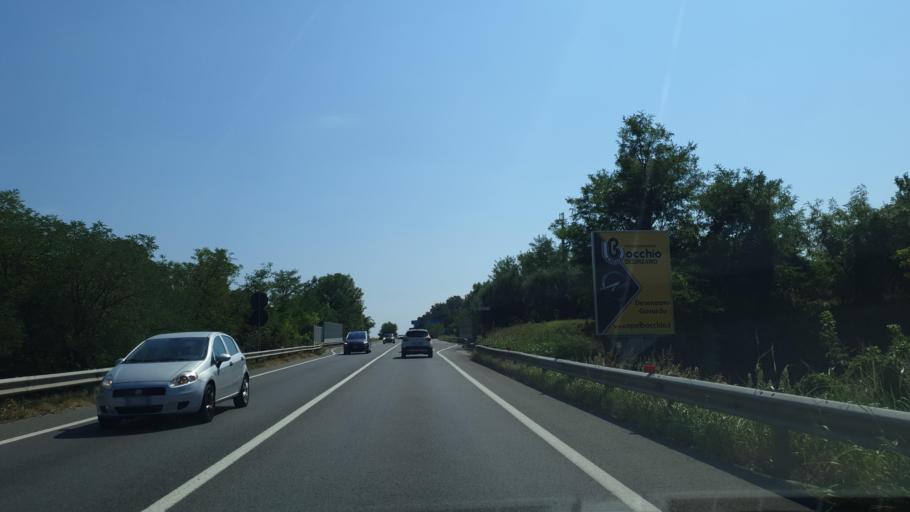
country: IT
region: Lombardy
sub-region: Provincia di Brescia
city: Lonato
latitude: 45.4646
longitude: 10.5040
